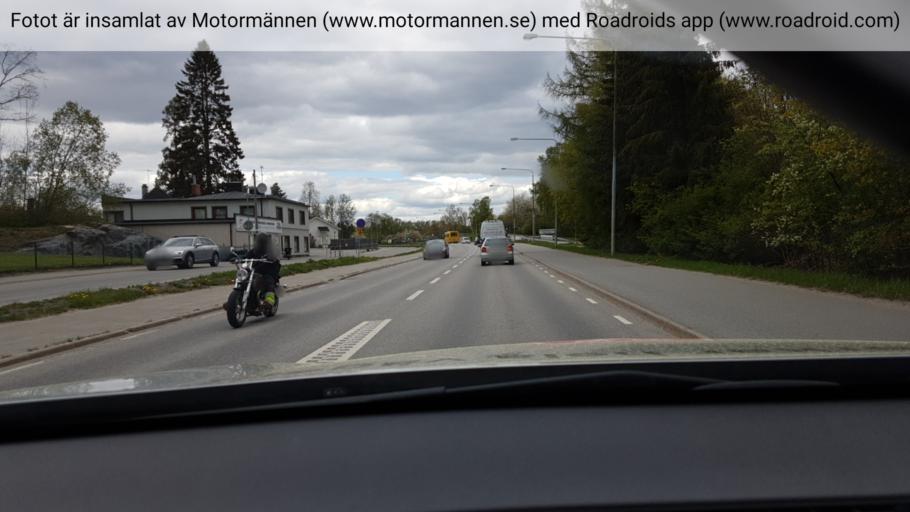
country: SE
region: Stockholm
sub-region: Tyreso Kommun
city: Bollmora
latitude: 59.2114
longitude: 18.2086
